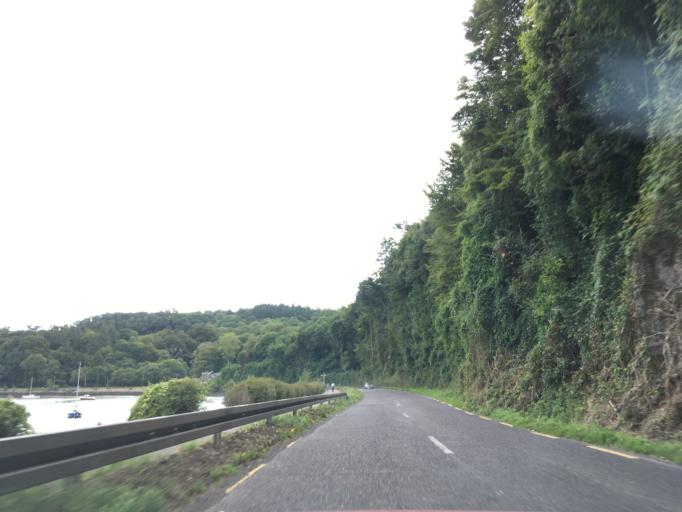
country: IE
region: Munster
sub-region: County Cork
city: Crosshaven
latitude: 51.8027
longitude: -8.3319
